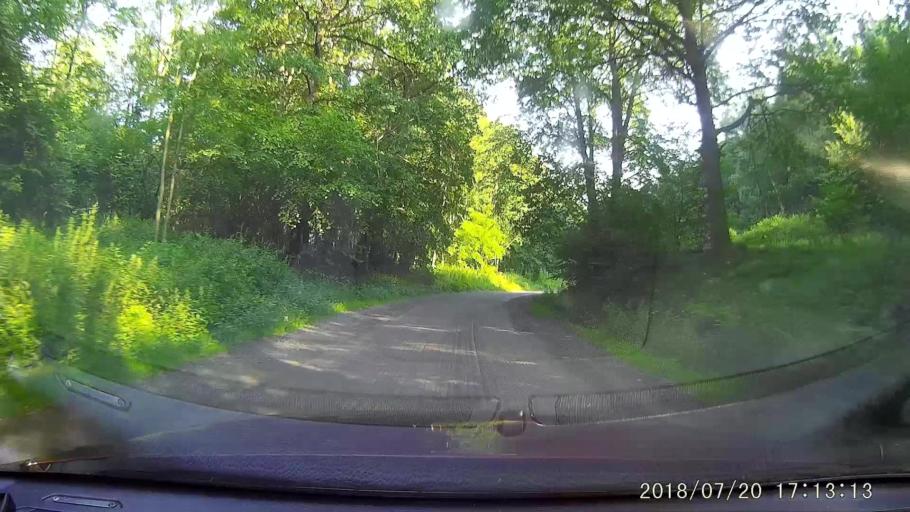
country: PL
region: Lower Silesian Voivodeship
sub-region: Powiat lubanski
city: Lesna
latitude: 51.0157
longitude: 15.2758
